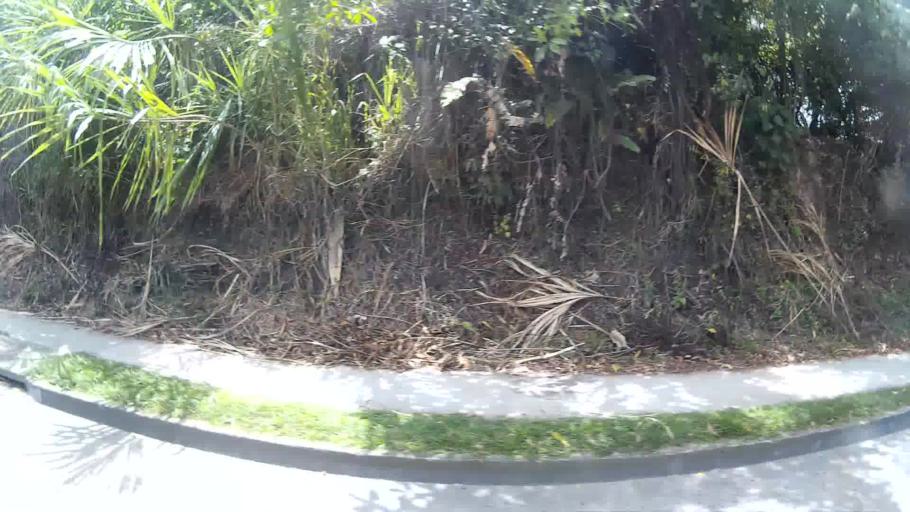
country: CO
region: Risaralda
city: Pereira
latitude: 4.8043
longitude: -75.7603
